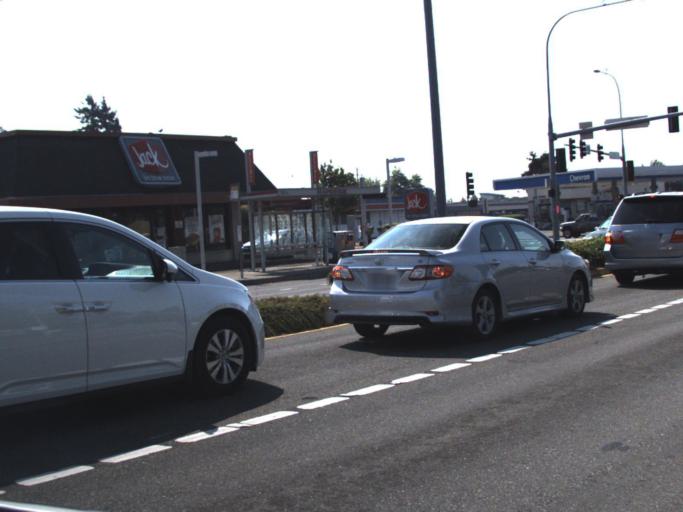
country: US
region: Washington
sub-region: King County
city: Federal Way
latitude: 47.3228
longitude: -122.3134
